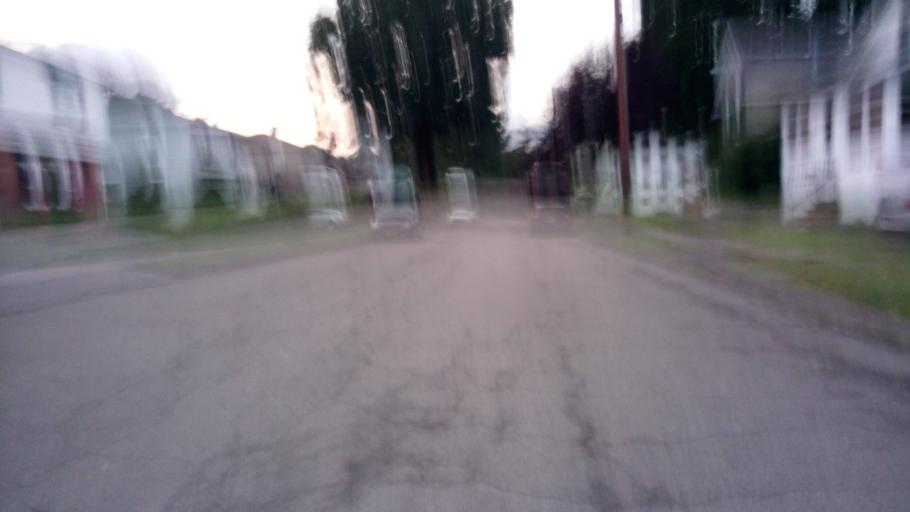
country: US
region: New York
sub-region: Chemung County
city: Elmira
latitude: 42.1033
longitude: -76.8243
